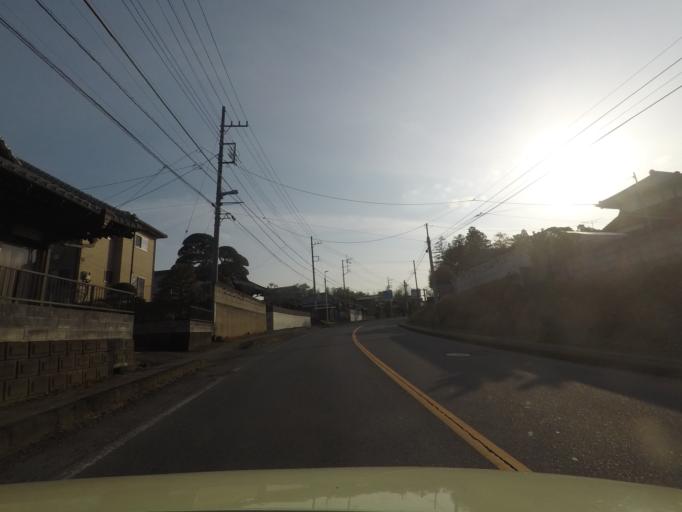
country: JP
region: Ibaraki
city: Okunoya
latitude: 36.2851
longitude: 140.4211
